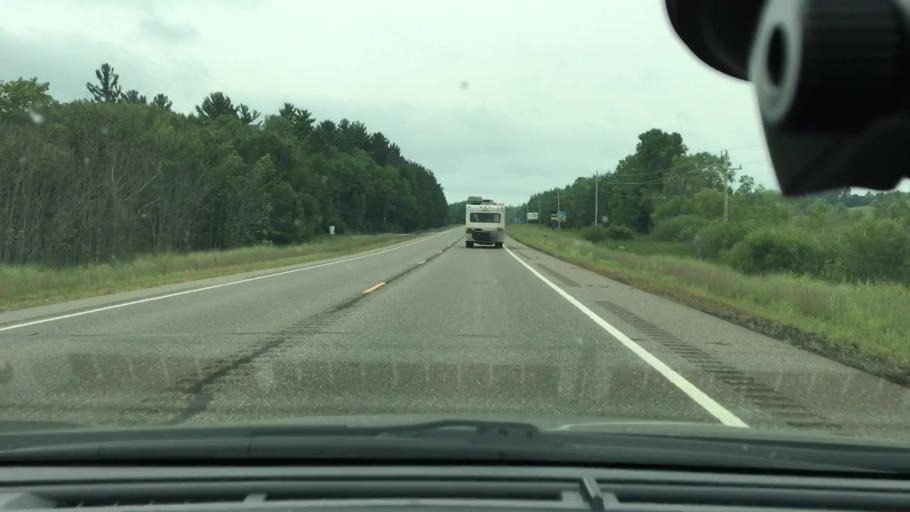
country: US
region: Minnesota
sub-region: Crow Wing County
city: Crosby
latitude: 46.5023
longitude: -93.9571
